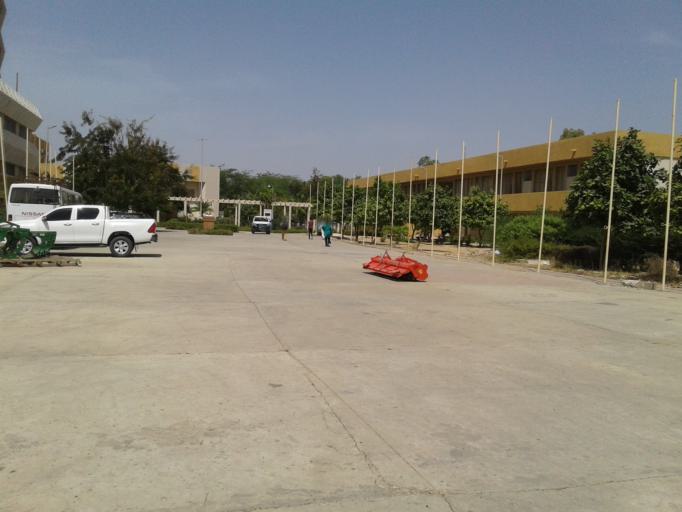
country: SN
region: Saint-Louis
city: Saint-Louis
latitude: 16.0611
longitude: -16.4222
